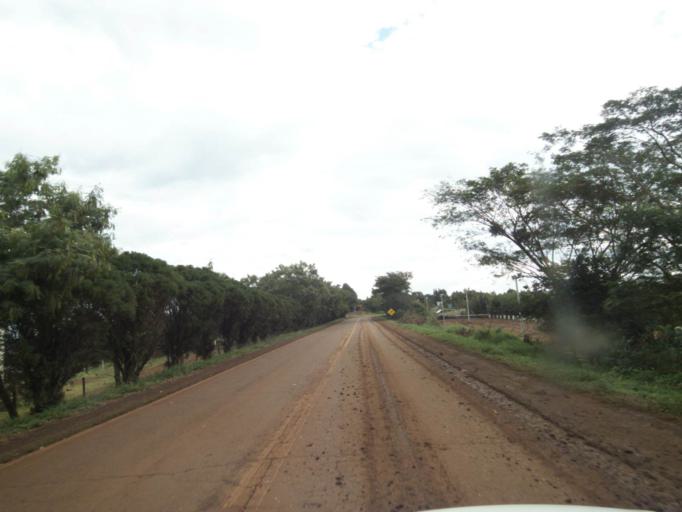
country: BR
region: Parana
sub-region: Marechal Candido Rondon
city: Marechal Candido Rondon
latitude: -24.7951
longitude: -54.2211
